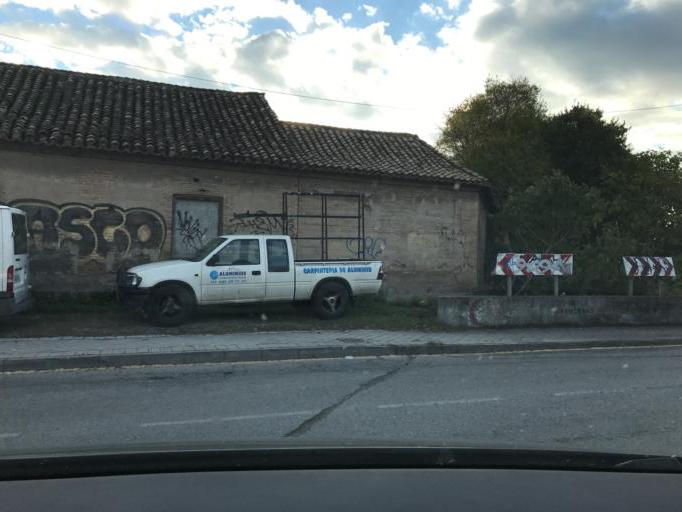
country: ES
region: Andalusia
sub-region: Provincia de Granada
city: Granada
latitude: 37.1813
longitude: -3.6197
